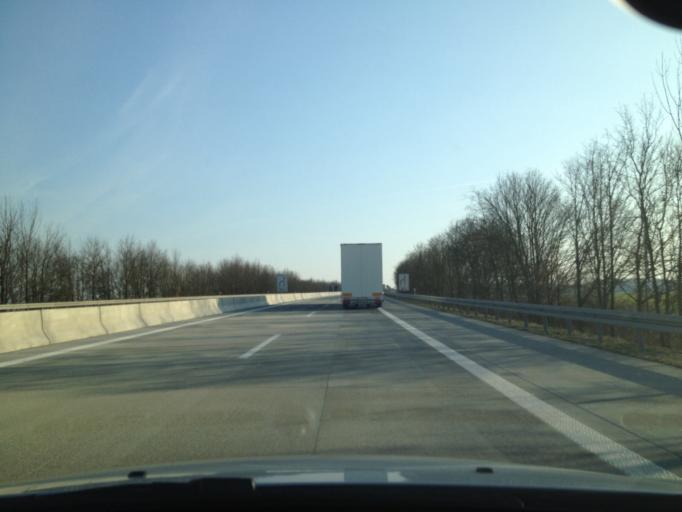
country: DE
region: Bavaria
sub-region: Regierungsbezirk Mittelfranken
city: Gollhofen
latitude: 49.5980
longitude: 10.1746
